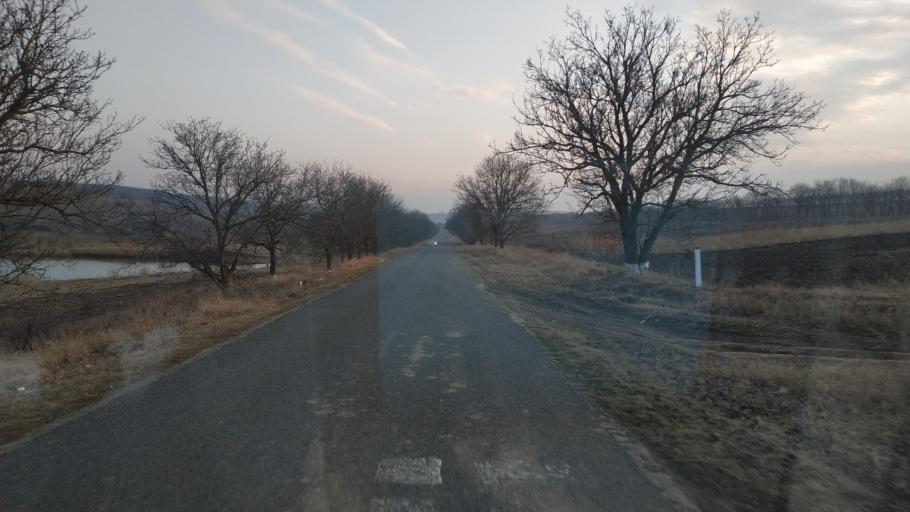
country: MD
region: Hincesti
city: Dancu
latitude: 46.6951
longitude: 28.3363
